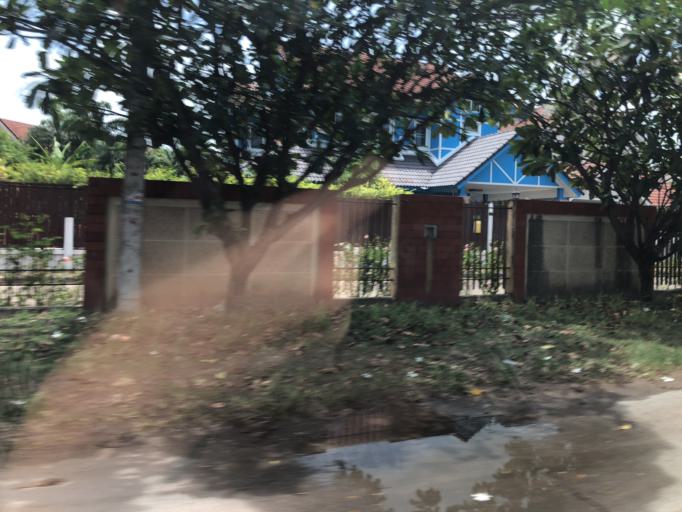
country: TH
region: Chon Buri
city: Si Racha
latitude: 13.1474
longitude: 100.9802
